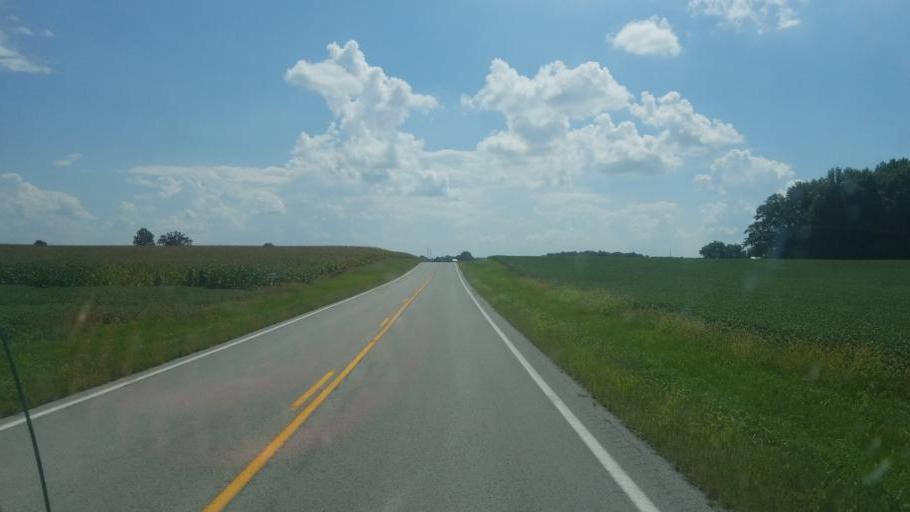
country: US
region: Ohio
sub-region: Hardin County
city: Forest
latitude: 40.8510
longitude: -83.4576
